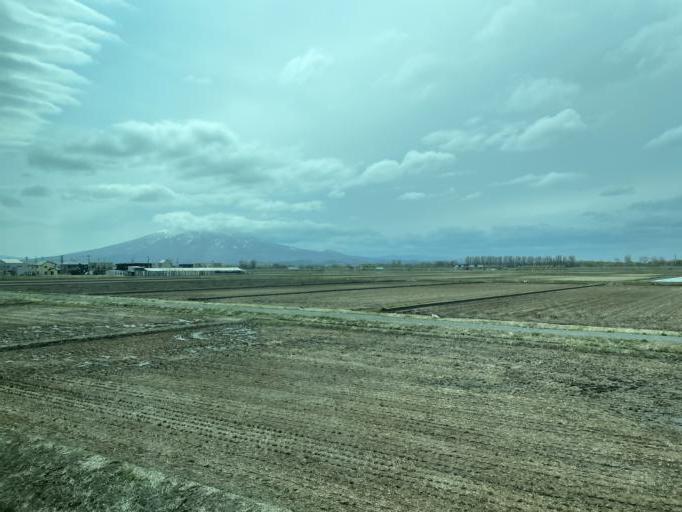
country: JP
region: Aomori
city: Goshogawara
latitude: 40.7724
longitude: 140.4339
